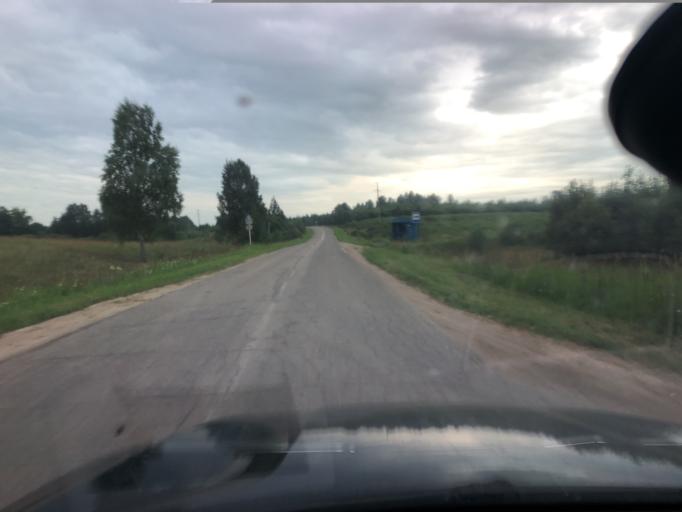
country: RU
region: Jaroslavl
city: Pereslavl'-Zalesskiy
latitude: 57.0144
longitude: 38.9601
